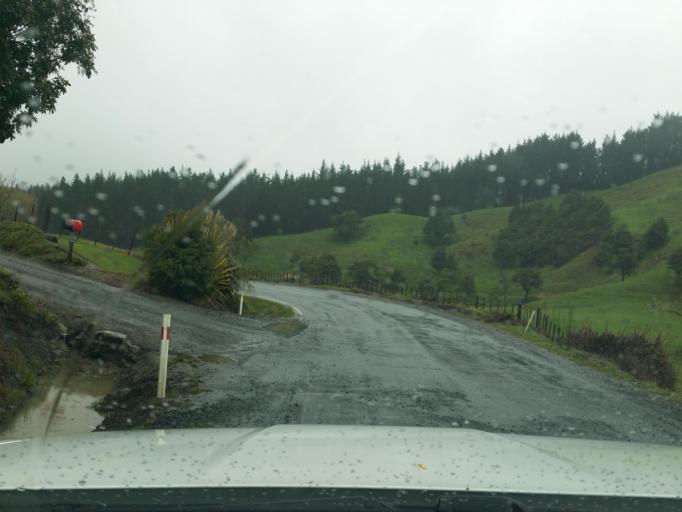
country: NZ
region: Northland
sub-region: Kaipara District
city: Dargaville
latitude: -35.8090
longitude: 173.9989
